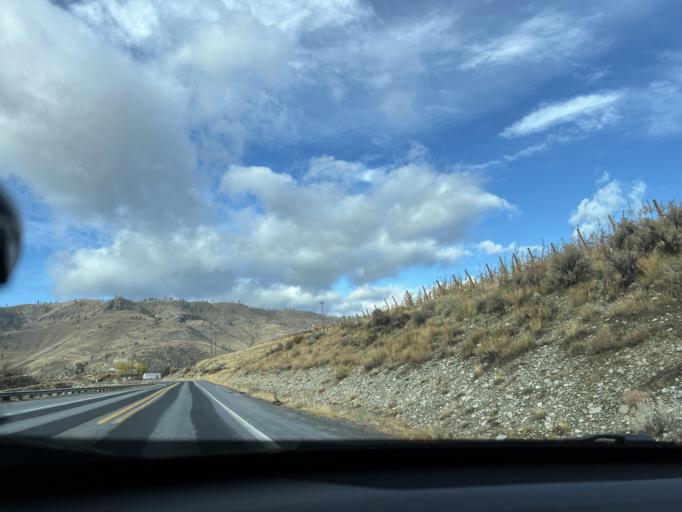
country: US
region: Washington
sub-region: Chelan County
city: Chelan
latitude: 47.8626
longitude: -119.9343
